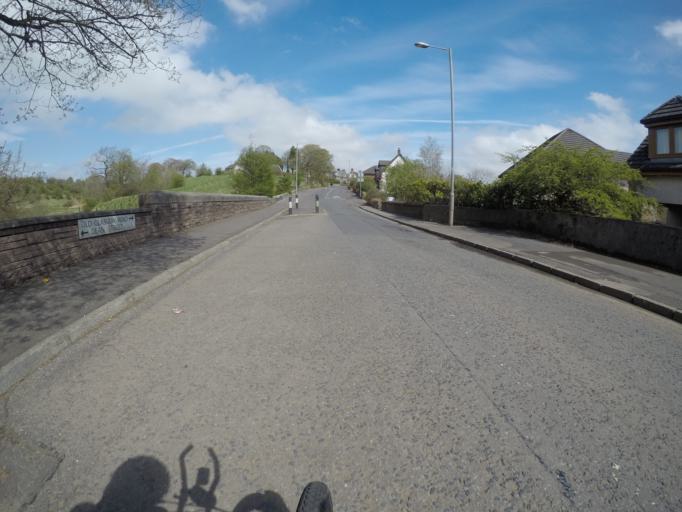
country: GB
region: Scotland
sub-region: East Ayrshire
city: Stewarton
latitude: 55.6852
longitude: -4.5068
